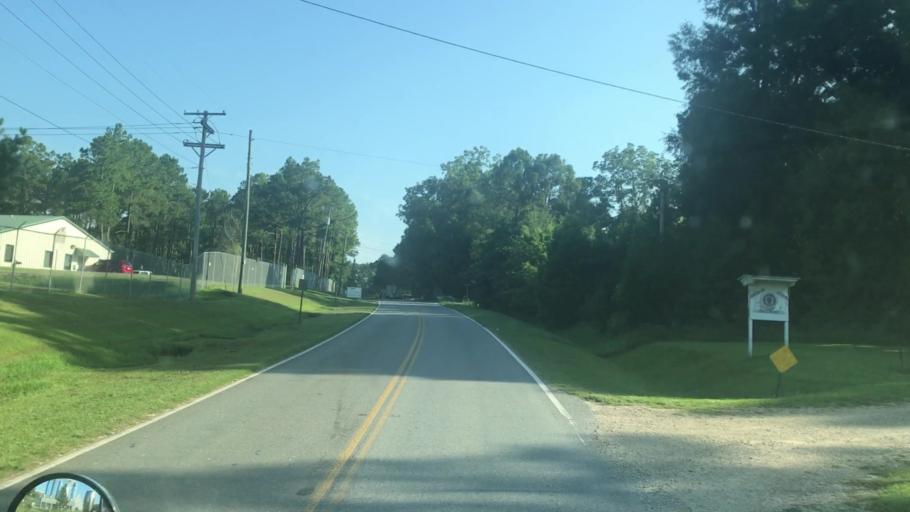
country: US
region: Florida
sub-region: Gadsden County
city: Quincy
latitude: 30.6030
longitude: -84.5722
